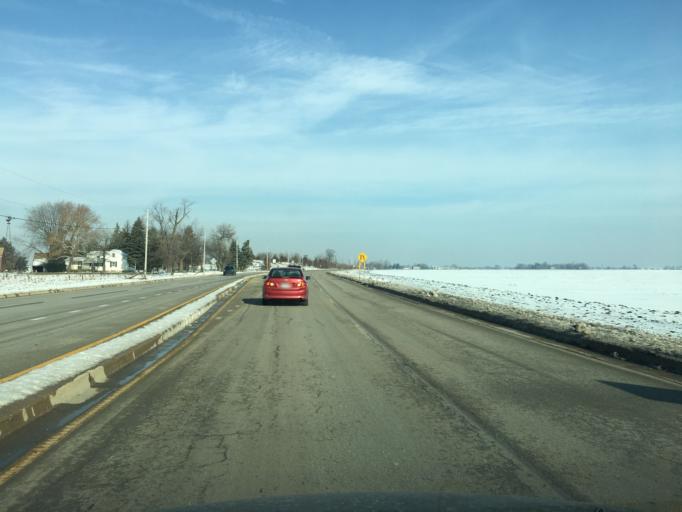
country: US
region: Illinois
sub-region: Will County
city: Plainfield
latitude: 41.6672
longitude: -88.1761
